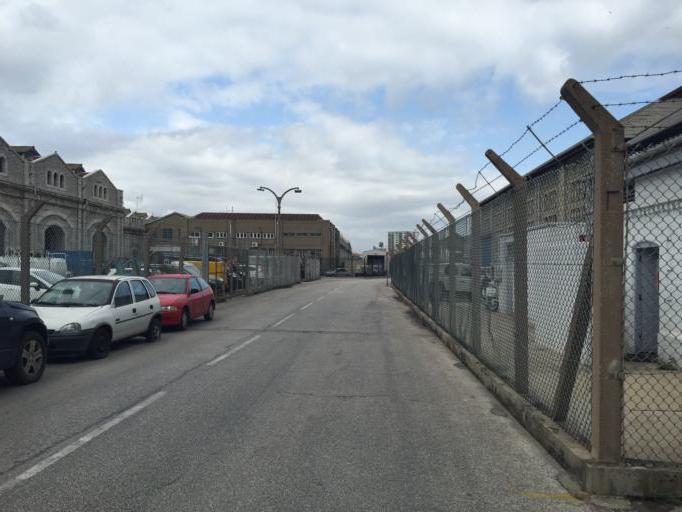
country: GI
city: Gibraltar
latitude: 36.1300
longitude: -5.3532
